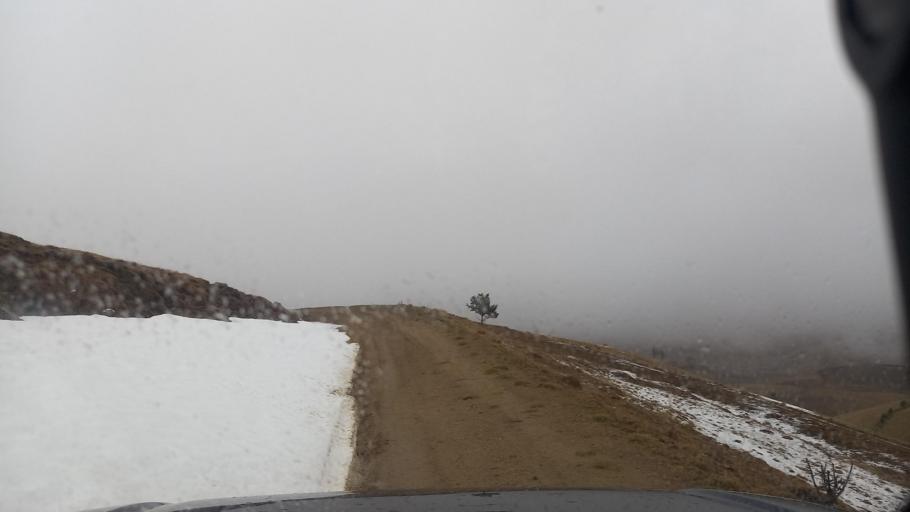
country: RU
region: Karachayevo-Cherkesiya
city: Uchkeken
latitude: 43.6038
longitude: 42.5627
